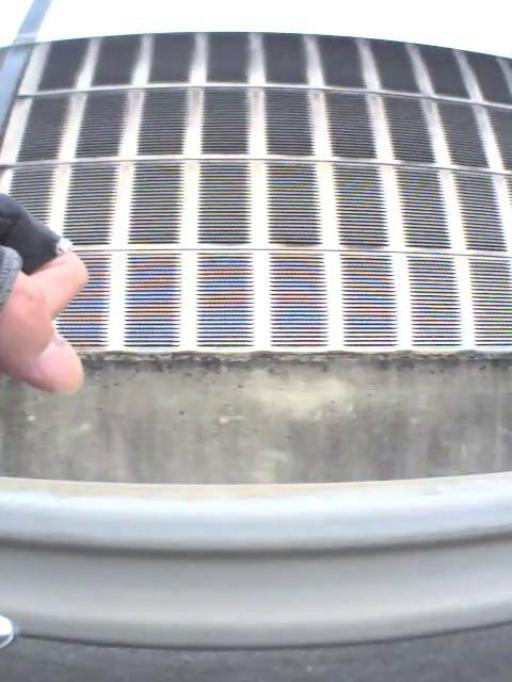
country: JP
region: Osaka
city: Hirakata
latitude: 34.8023
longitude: 135.6333
